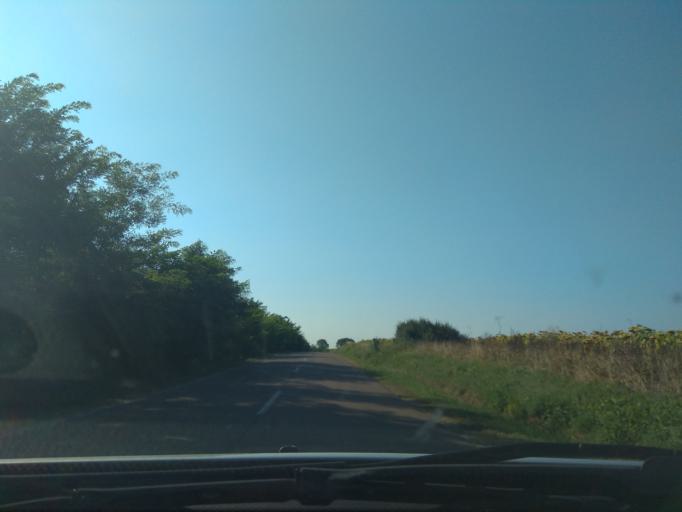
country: HU
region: Borsod-Abauj-Zemplen
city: Emod
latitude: 47.9564
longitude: 20.8075
